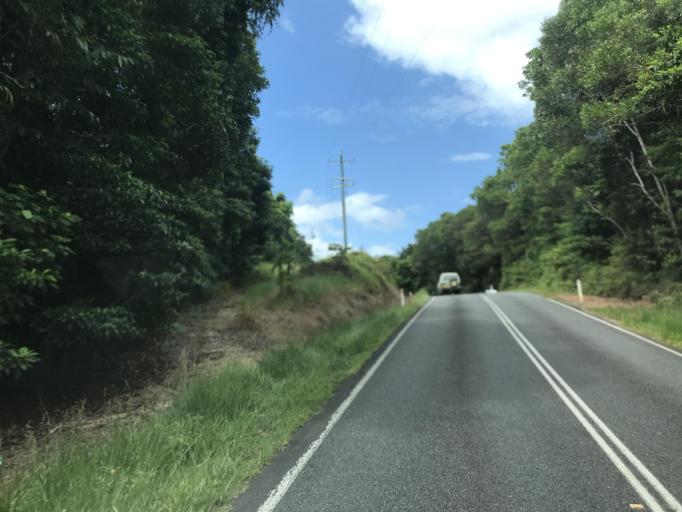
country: AU
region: Queensland
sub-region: Cassowary Coast
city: Innisfail
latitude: -17.8302
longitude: 146.0552
